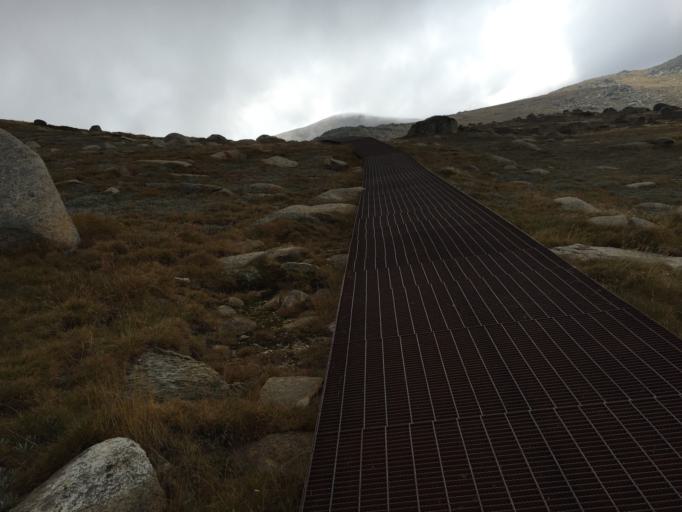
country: AU
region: New South Wales
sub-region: Snowy River
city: Jindabyne
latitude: -36.4697
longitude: 148.2720
